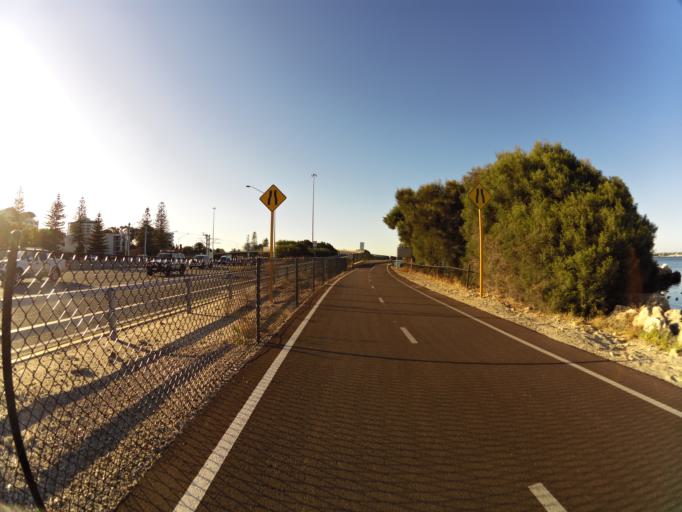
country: AU
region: Western Australia
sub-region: City of Perth
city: West Perth
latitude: -31.9711
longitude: 115.8470
